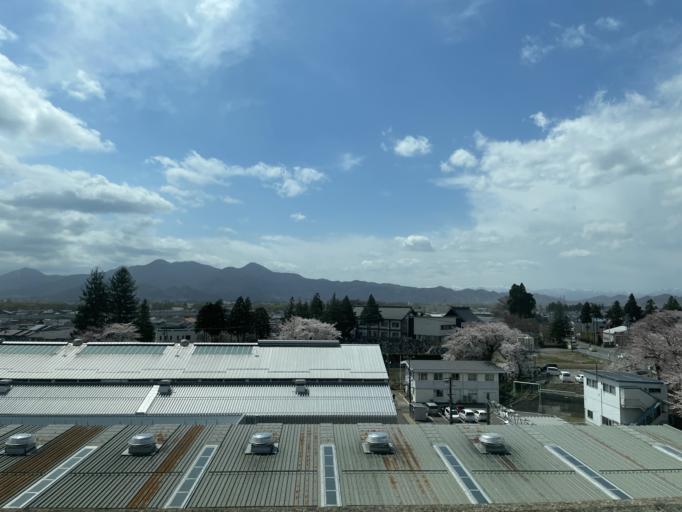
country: JP
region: Iwate
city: Morioka-shi
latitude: 39.7126
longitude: 141.1238
